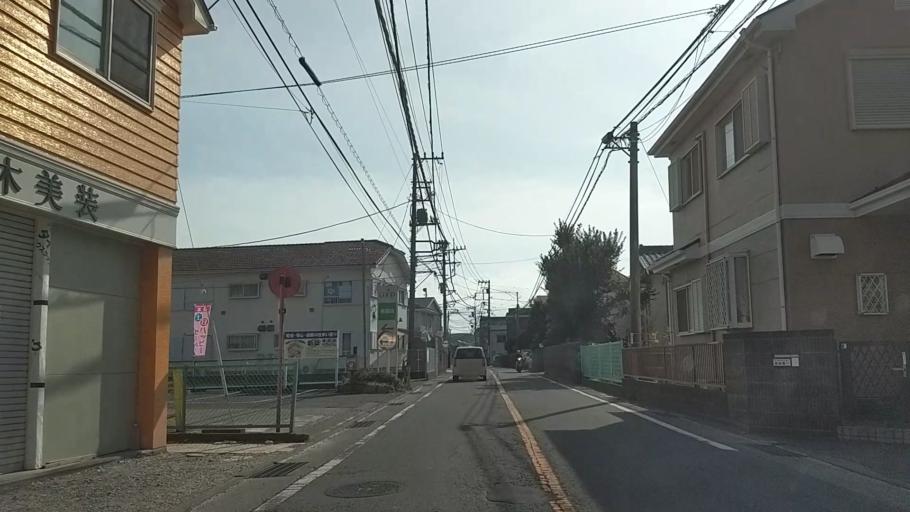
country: JP
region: Kanagawa
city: Chigasaki
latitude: 35.3406
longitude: 139.3827
